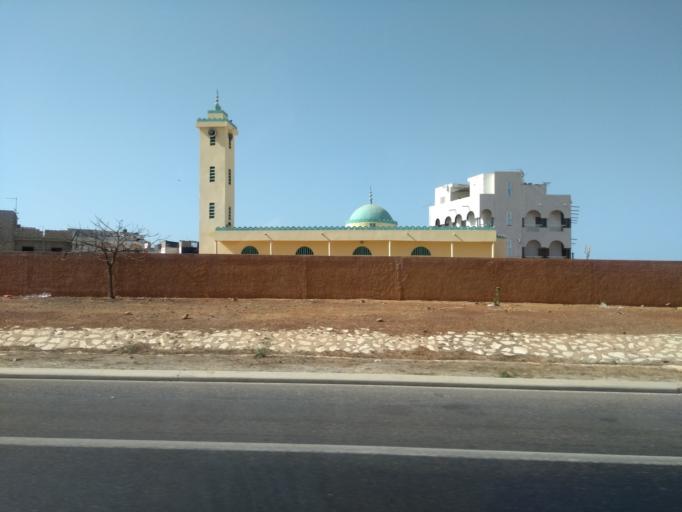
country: SN
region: Dakar
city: Pikine
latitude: 14.7545
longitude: -17.3667
